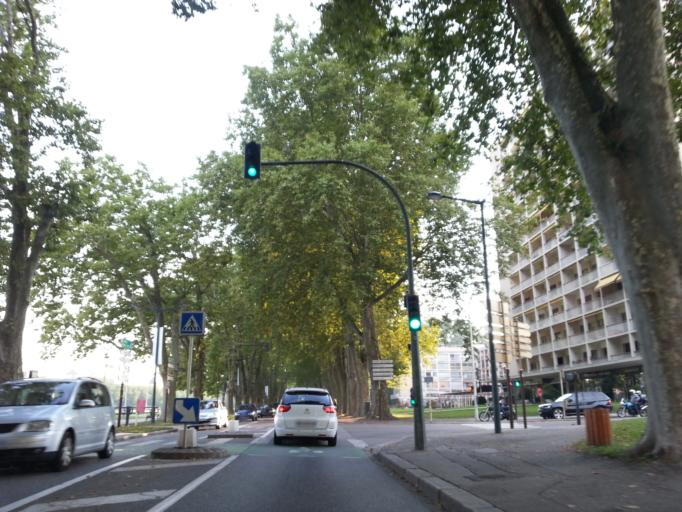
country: FR
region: Rhone-Alpes
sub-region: Departement de la Haute-Savoie
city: Annecy-le-Vieux
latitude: 45.9036
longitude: 6.1365
